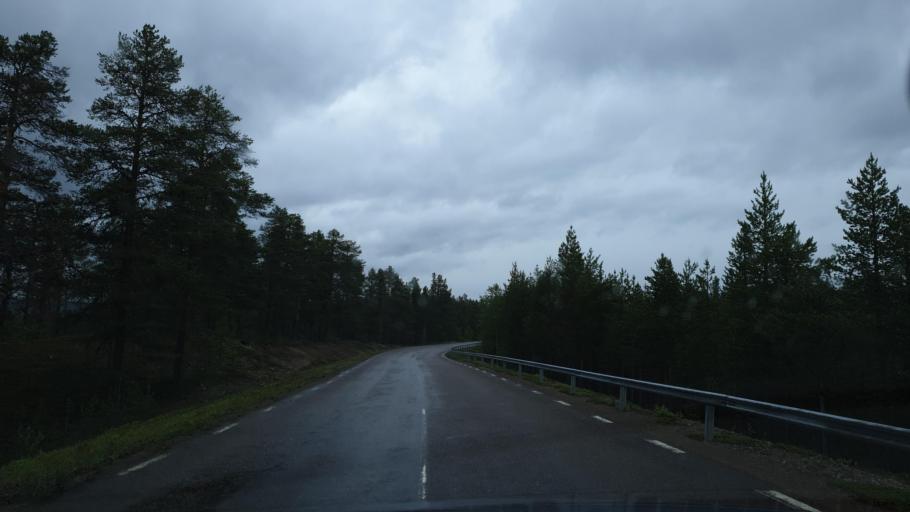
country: SE
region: Norrbotten
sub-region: Kiruna Kommun
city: Kiruna
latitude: 67.8806
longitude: 20.9966
